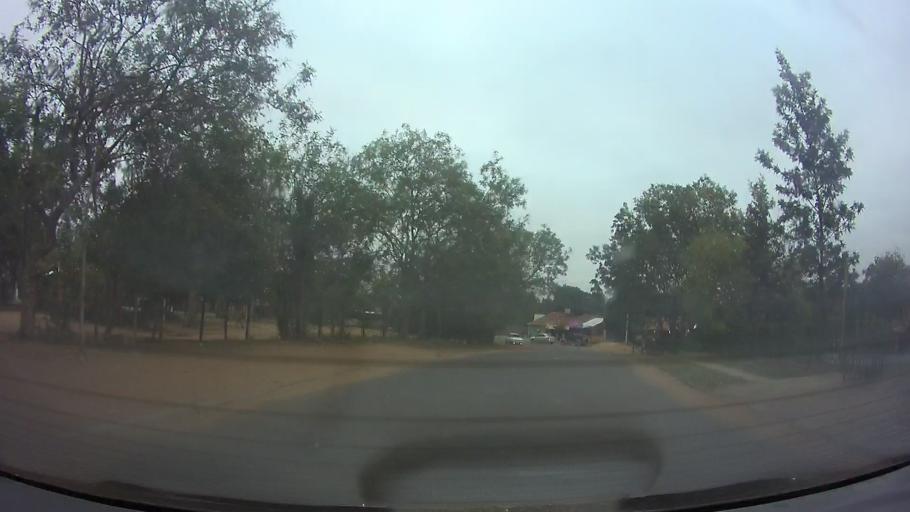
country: PY
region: Central
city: Limpio
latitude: -25.1517
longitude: -57.4562
